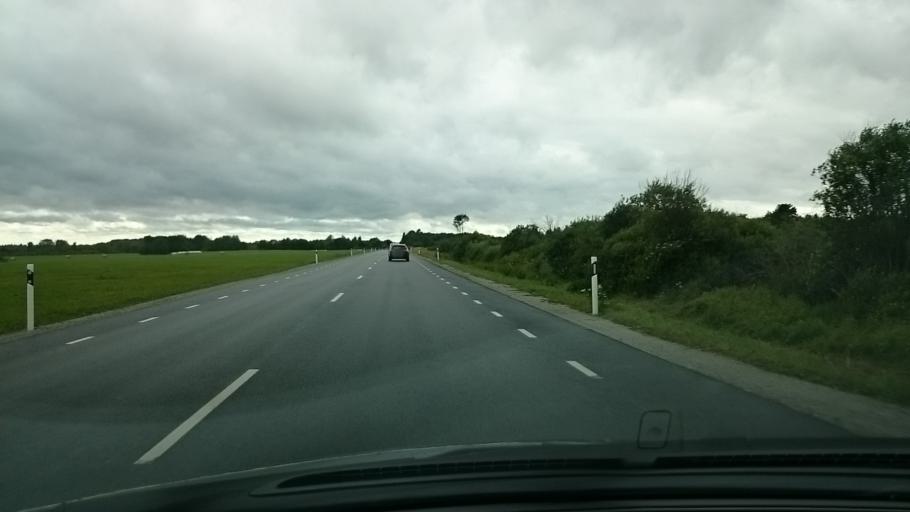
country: EE
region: Harju
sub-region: Keila linn
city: Keila
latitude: 59.3034
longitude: 24.3619
